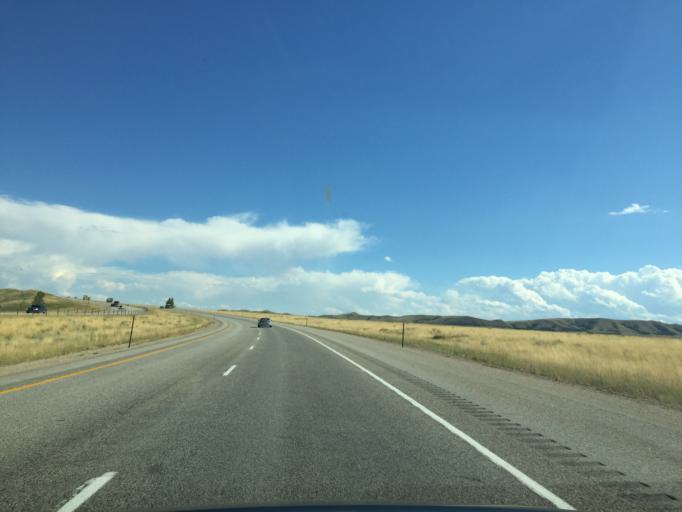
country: US
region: Wyoming
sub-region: Sheridan County
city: Sheridan
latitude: 44.6041
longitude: -106.8479
